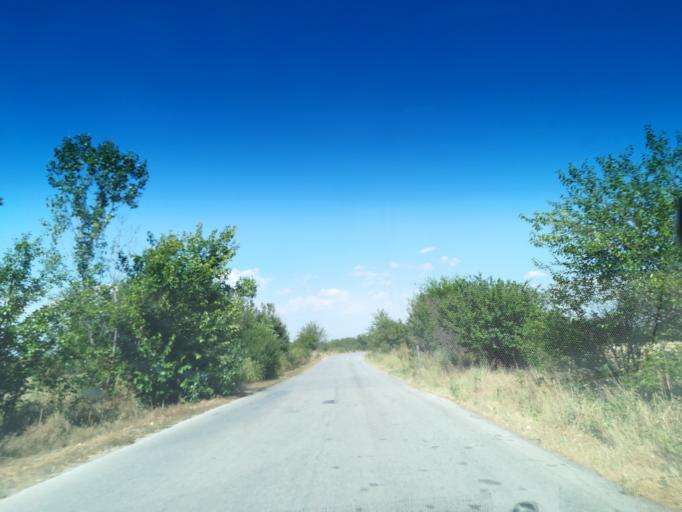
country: BG
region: Stara Zagora
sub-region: Obshtina Chirpan
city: Chirpan
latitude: 42.0702
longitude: 25.1802
